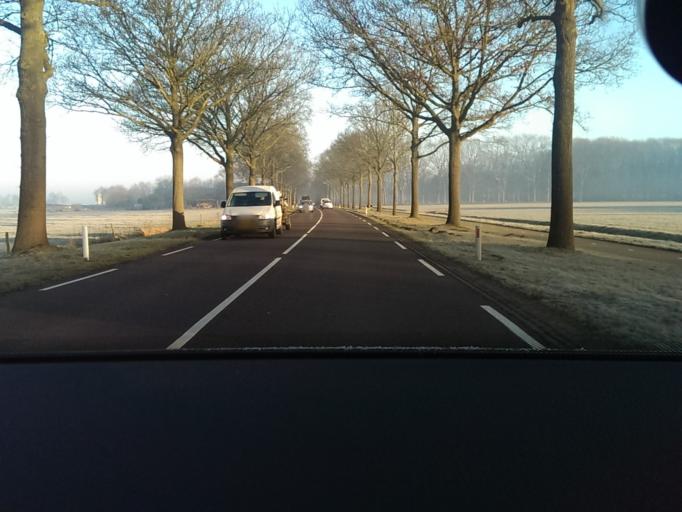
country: NL
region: Overijssel
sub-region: Gemeente Twenterand
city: Vroomshoop
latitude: 52.4176
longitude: 6.5519
